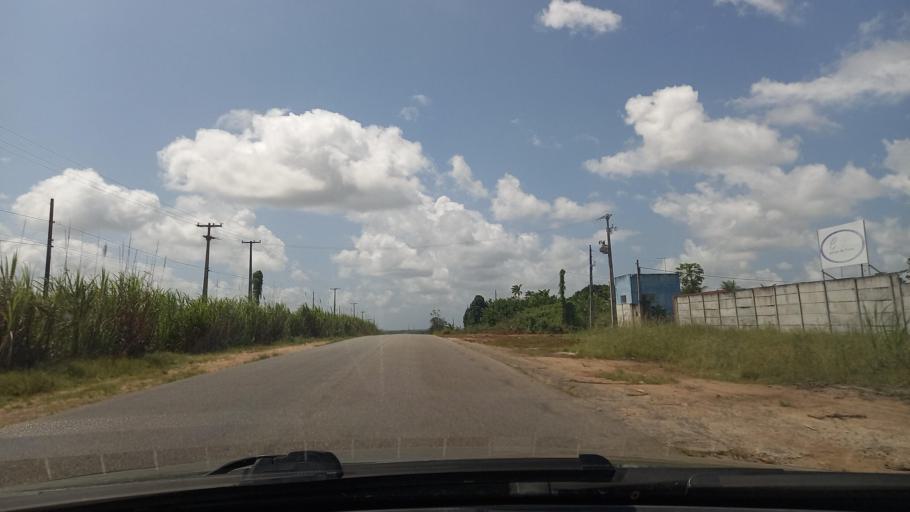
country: BR
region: Pernambuco
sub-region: Goiana
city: Goiana
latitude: -7.5579
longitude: -35.0319
